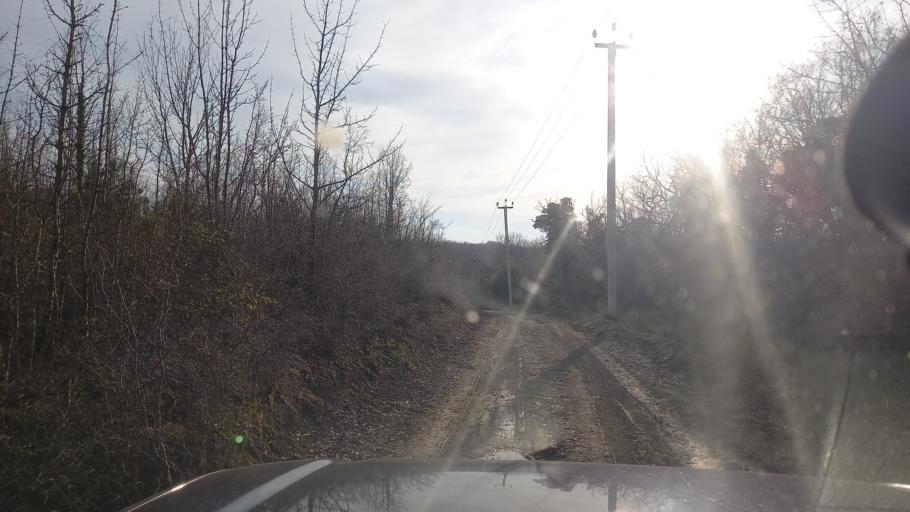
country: RU
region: Krasnodarskiy
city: Arkhipo-Osipovka
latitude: 44.3627
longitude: 38.5689
